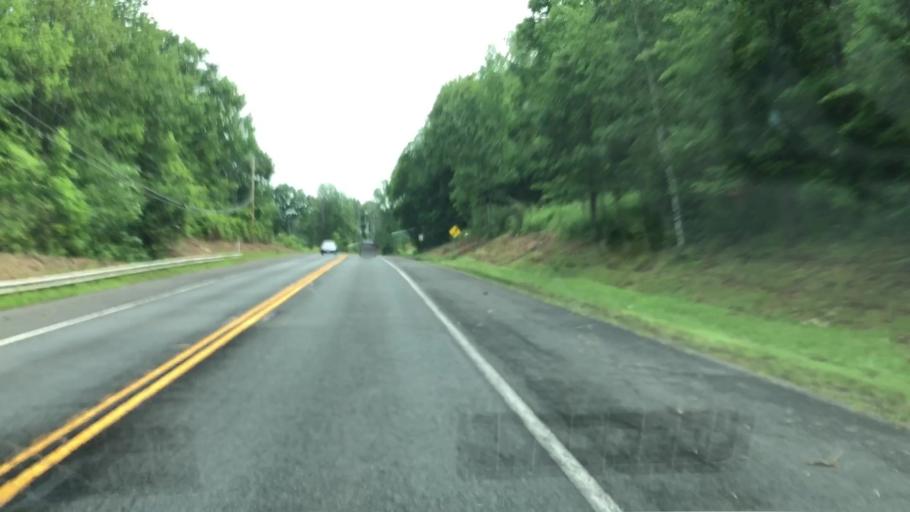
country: US
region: Massachusetts
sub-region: Berkshire County
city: Lanesborough
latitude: 42.5450
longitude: -73.1700
